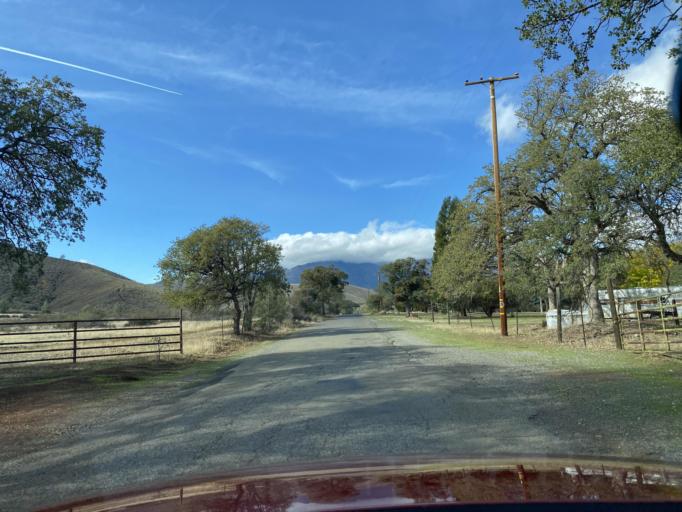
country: US
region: California
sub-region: Lake County
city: Lucerne
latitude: 39.3691
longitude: -122.6037
